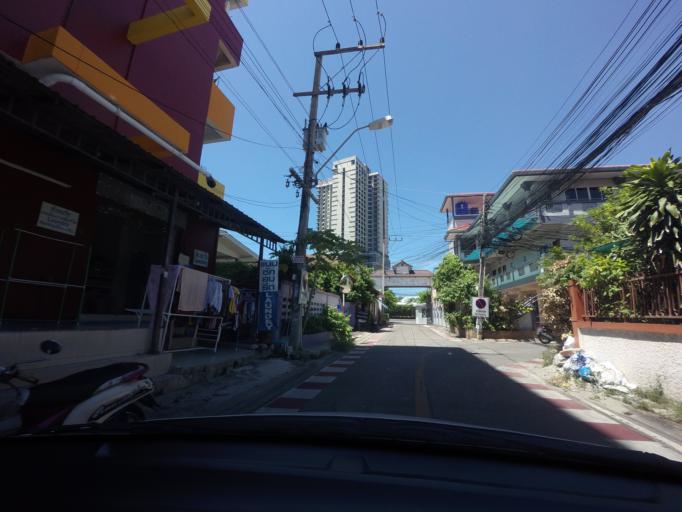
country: TH
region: Chon Buri
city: Phatthaya
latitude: 12.9550
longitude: 100.8932
